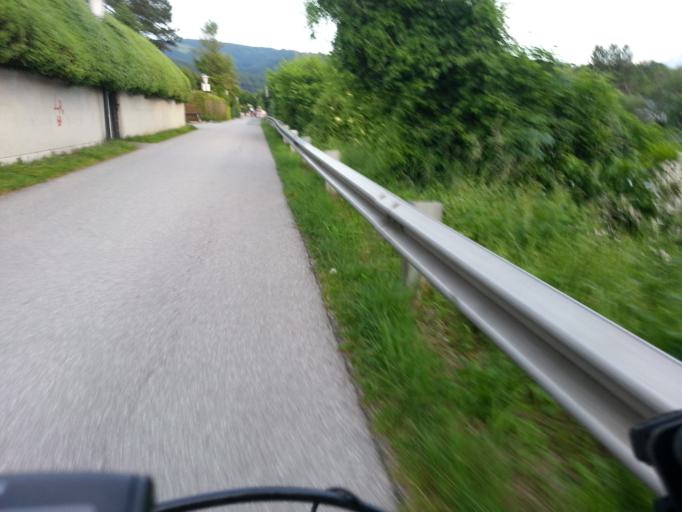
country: AT
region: Salzburg
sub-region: Salzburg Stadt
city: Salzburg
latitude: 47.7876
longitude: 13.0729
